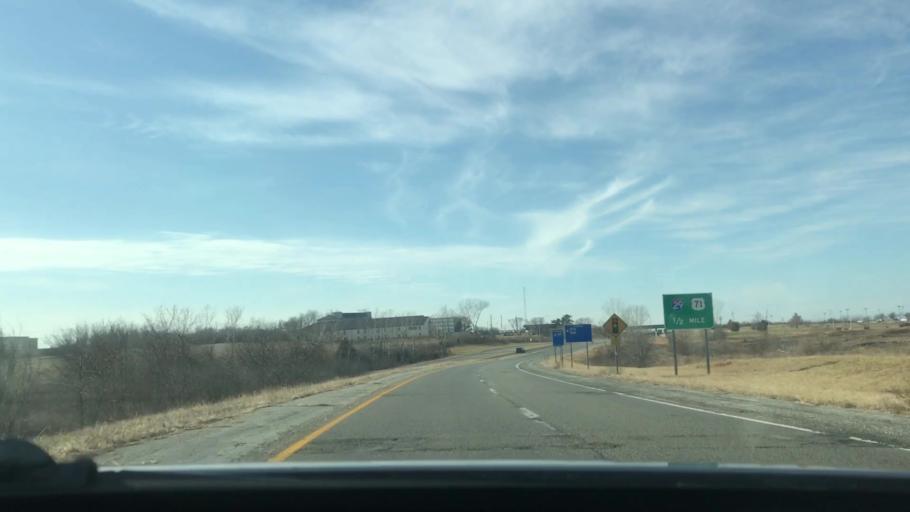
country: US
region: Missouri
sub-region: Platte County
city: Weatherby Lake
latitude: 39.3116
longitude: -94.6766
